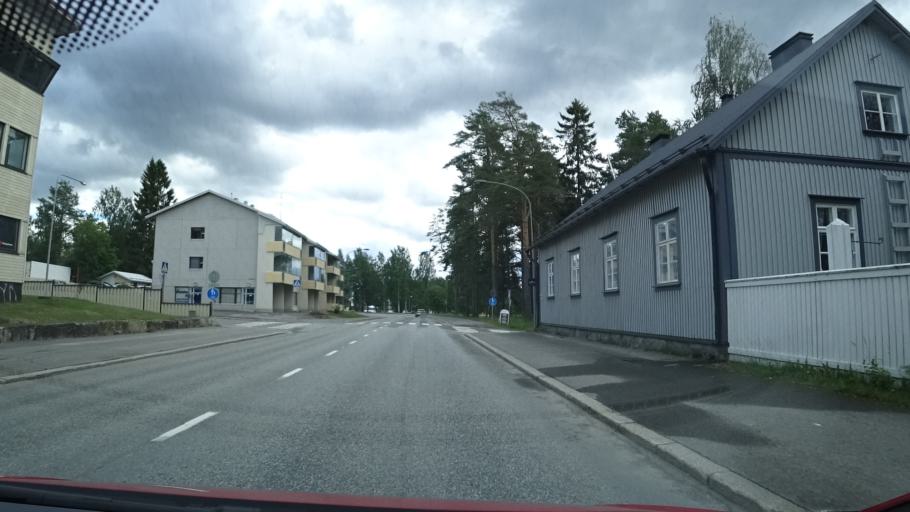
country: FI
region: North Karelia
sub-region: Pielisen Karjala
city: Nurmes
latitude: 63.5428
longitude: 29.1344
